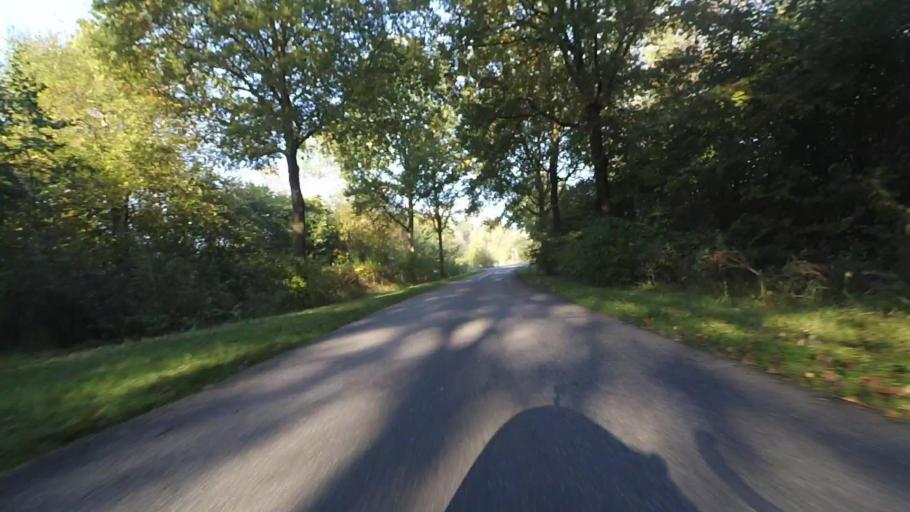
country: NL
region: Flevoland
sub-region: Gemeente Zeewolde
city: Zeewolde
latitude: 52.3039
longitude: 5.5104
